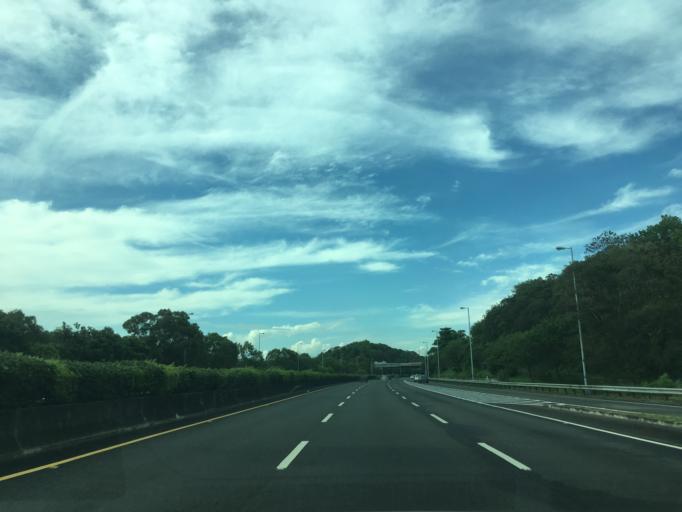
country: TW
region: Taiwan
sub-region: Chiayi
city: Jiayi Shi
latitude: 23.5231
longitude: 120.4851
